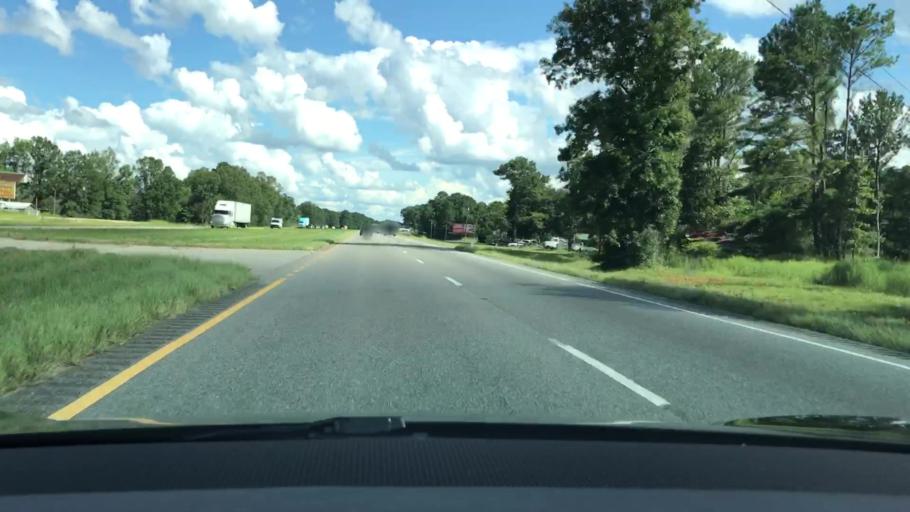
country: US
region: Alabama
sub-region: Montgomery County
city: Taylor
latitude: 32.0499
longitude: -86.0419
